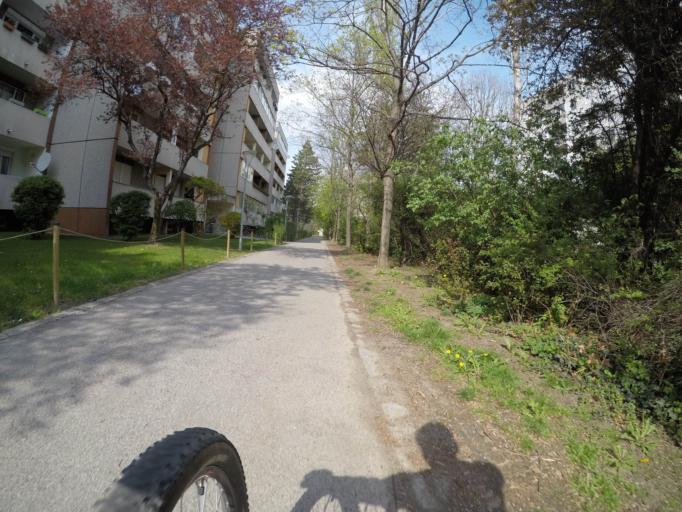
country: AT
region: Lower Austria
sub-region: Politischer Bezirk Modling
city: Wiener Neudorf
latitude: 48.0888
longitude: 16.3098
